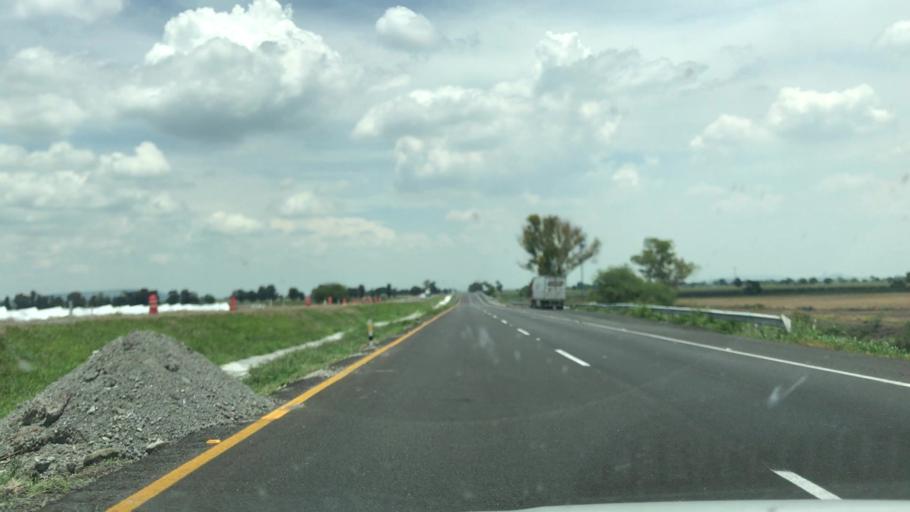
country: MX
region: Guanajuato
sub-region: Salamanca
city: San Vicente de Flores
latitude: 20.6387
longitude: -101.2629
